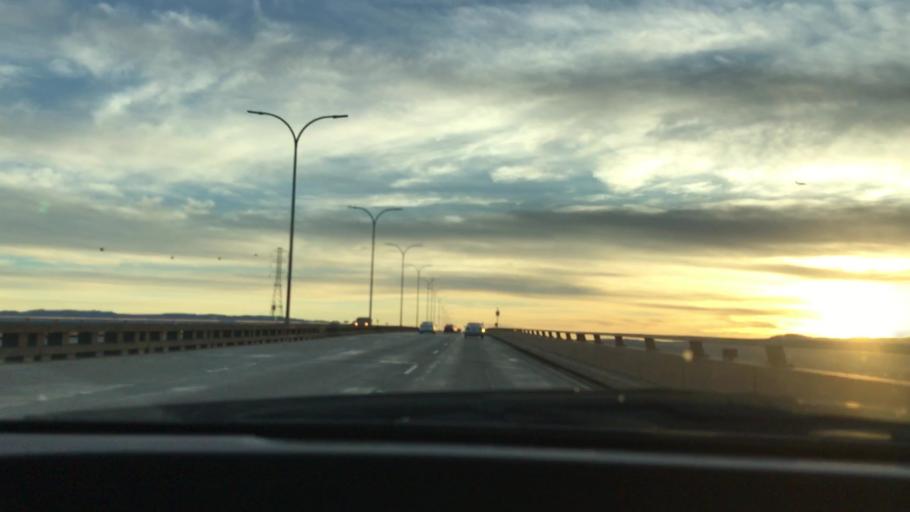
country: US
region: California
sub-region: San Mateo County
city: Foster City
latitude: 37.5859
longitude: -122.2491
